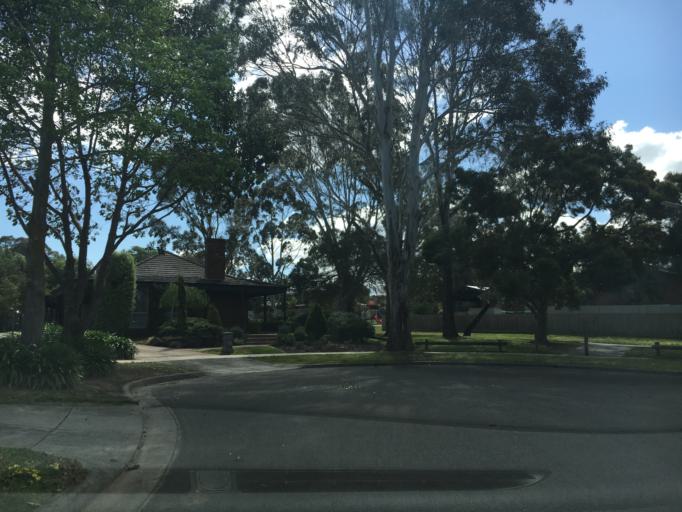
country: AU
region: Victoria
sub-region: Whitehorse
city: Vermont South
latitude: -37.8865
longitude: 145.1844
